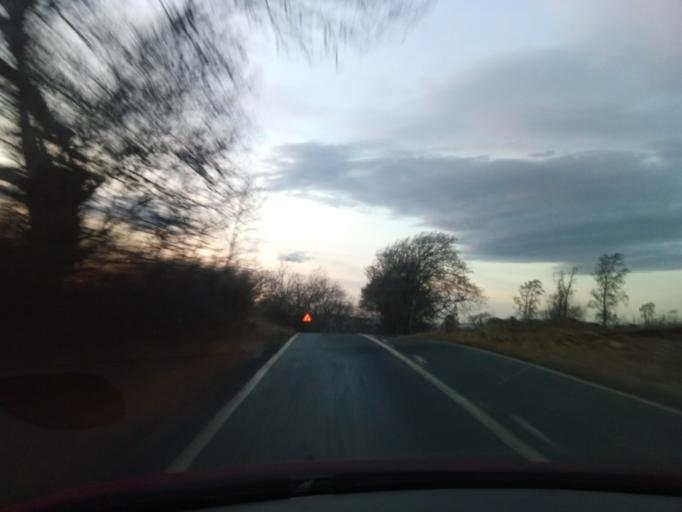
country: GB
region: England
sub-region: Northumberland
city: Otterburn
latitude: 55.2294
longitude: -2.1687
